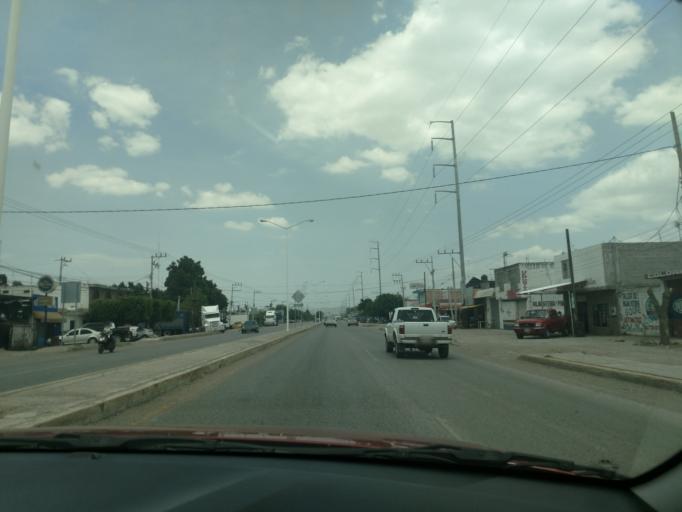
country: MX
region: San Luis Potosi
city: Rio Verde
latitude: 21.9222
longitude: -99.9752
